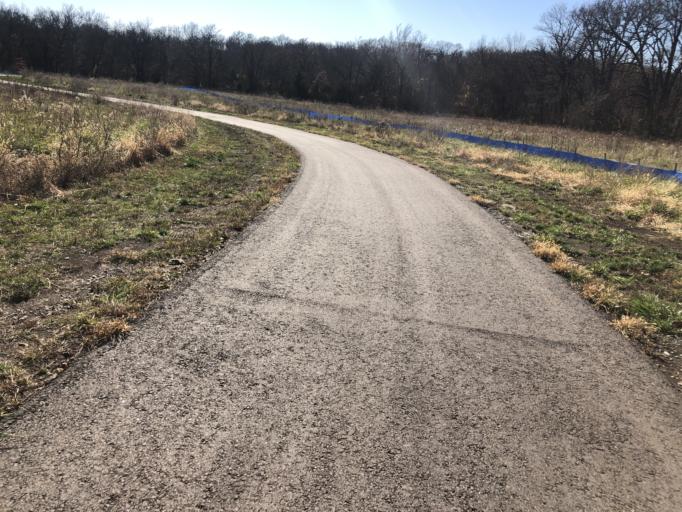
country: US
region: Kansas
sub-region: Johnson County
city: Gardner
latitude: 38.8754
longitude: -94.9540
